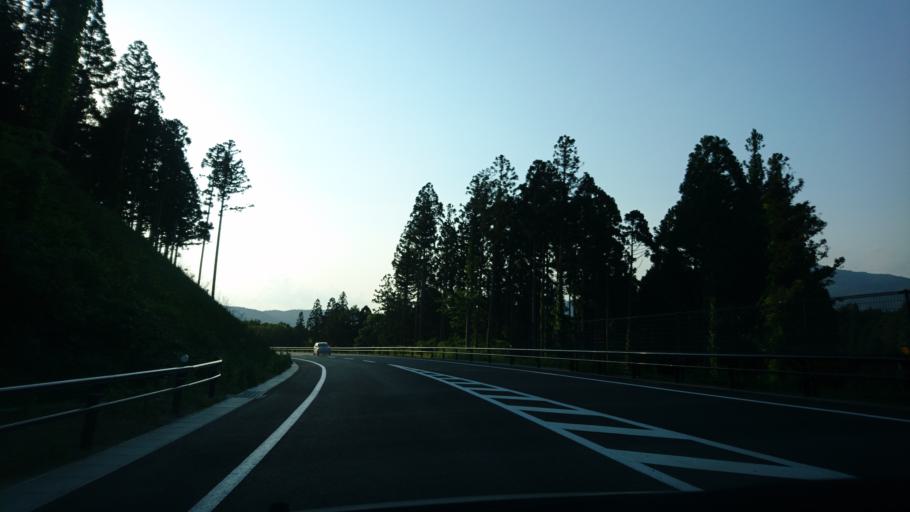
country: JP
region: Iwate
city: Ofunato
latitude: 38.9309
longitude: 141.4516
